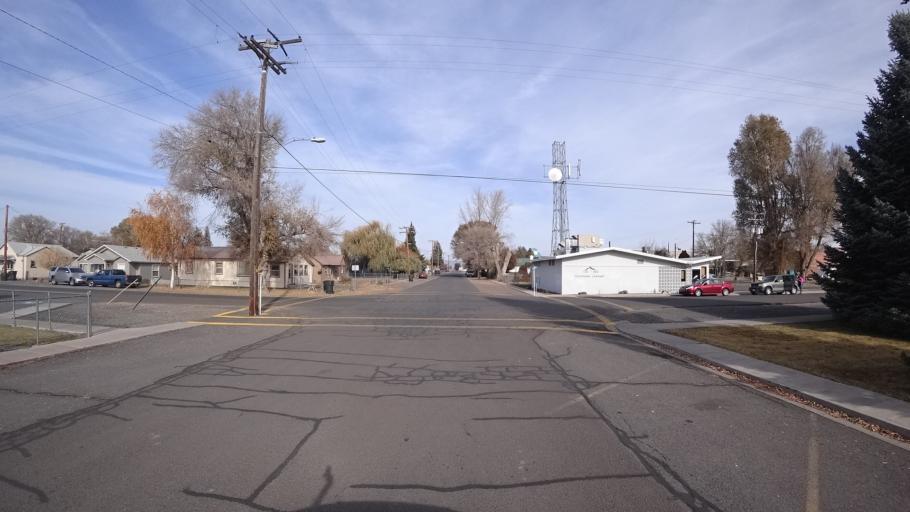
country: US
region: California
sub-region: Siskiyou County
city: Tulelake
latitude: 41.9559
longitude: -121.4780
